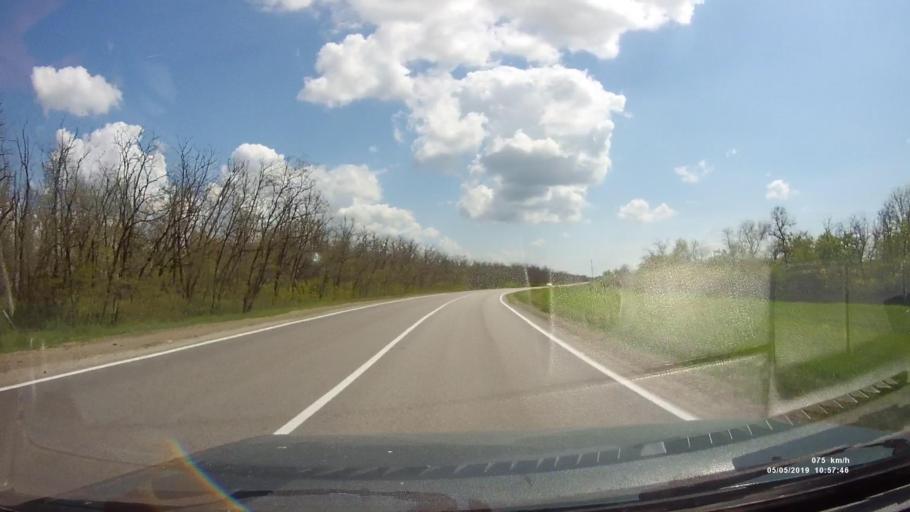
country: RU
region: Rostov
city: Ust'-Donetskiy
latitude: 47.6714
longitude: 40.8421
